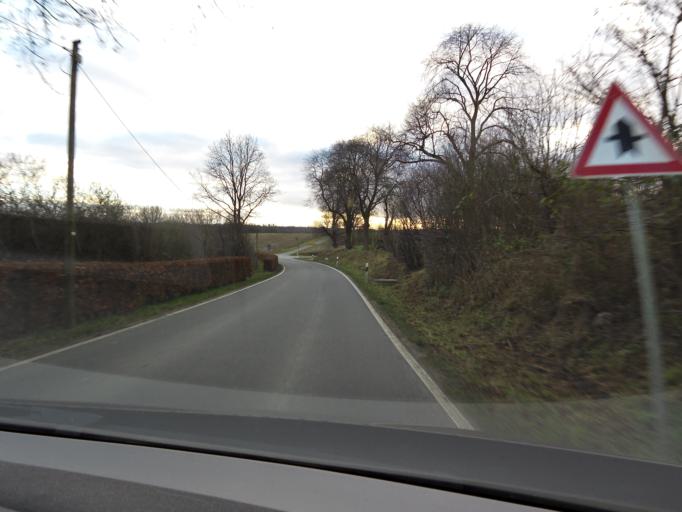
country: DE
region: Schleswig-Holstein
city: Klein Zecher
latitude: 53.5812
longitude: 10.8915
